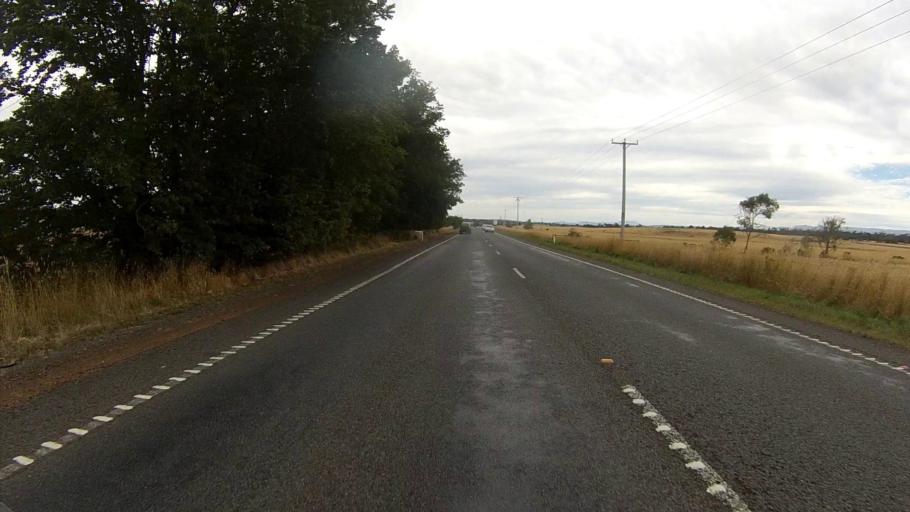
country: AU
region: Tasmania
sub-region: Northern Midlands
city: Evandale
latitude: -41.8648
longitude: 147.4575
